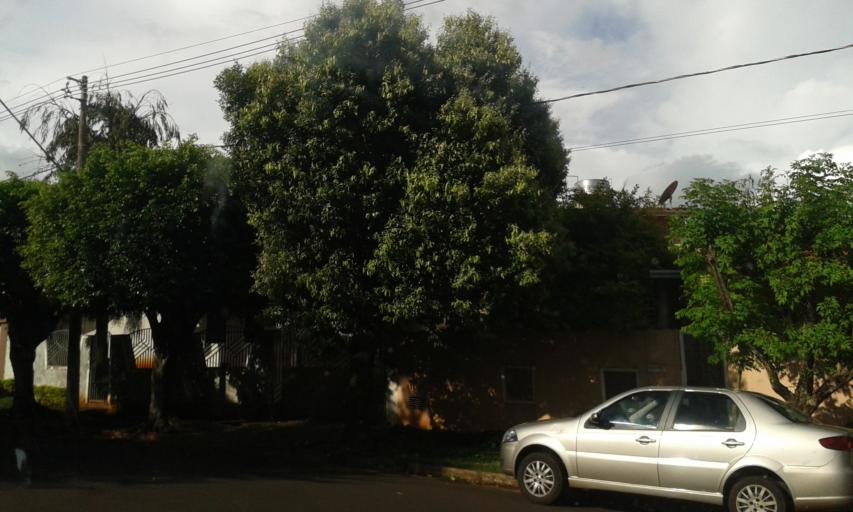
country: BR
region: Minas Gerais
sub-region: Ituiutaba
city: Ituiutaba
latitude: -18.9708
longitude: -49.4516
